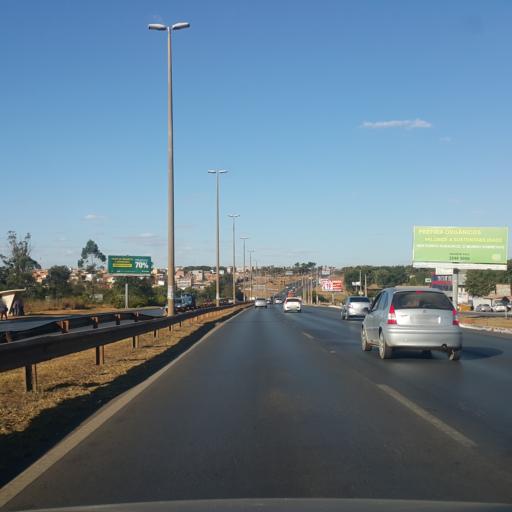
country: BR
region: Federal District
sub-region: Brasilia
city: Brasilia
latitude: -15.7868
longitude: -48.0077
